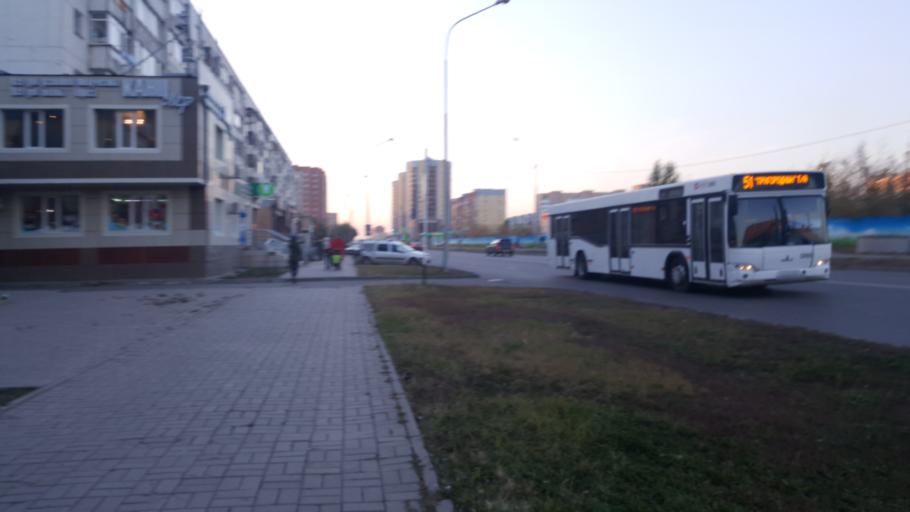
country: KZ
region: Astana Qalasy
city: Astana
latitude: 51.1552
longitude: 71.5022
